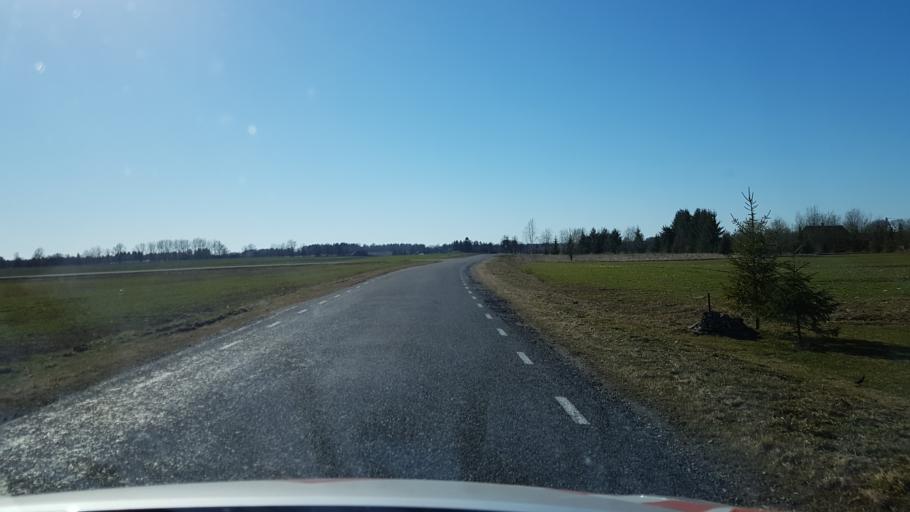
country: EE
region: Laeaene-Virumaa
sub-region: Haljala vald
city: Haljala
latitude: 59.4350
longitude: 26.2104
